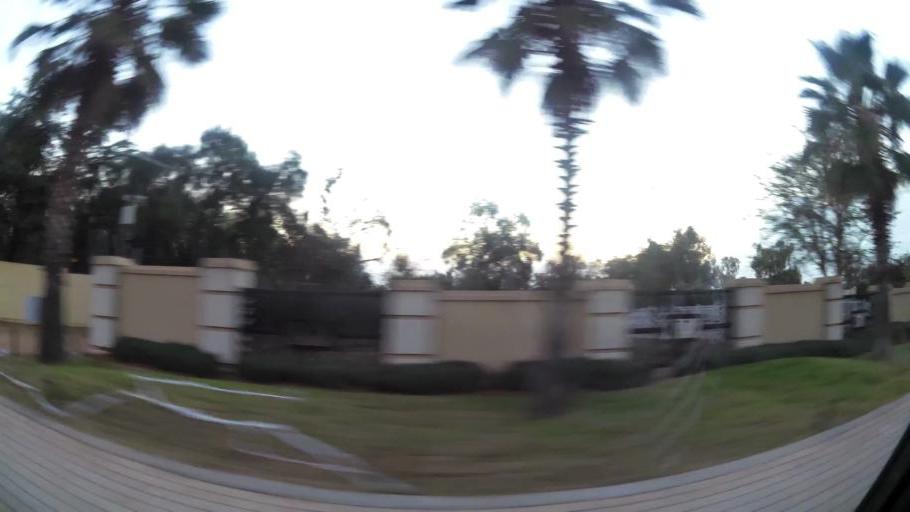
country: ZA
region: Gauteng
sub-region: City of Johannesburg Metropolitan Municipality
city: Diepsloot
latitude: -25.9671
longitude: 28.0655
